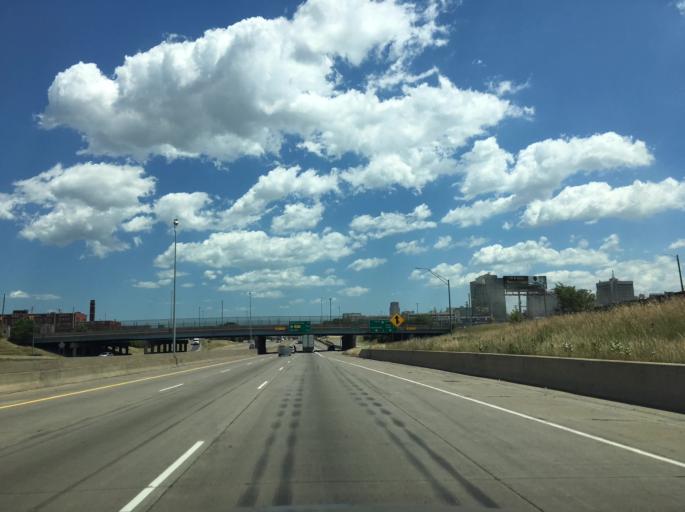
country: US
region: Michigan
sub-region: Wayne County
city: Detroit
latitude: 42.3339
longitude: -83.0705
